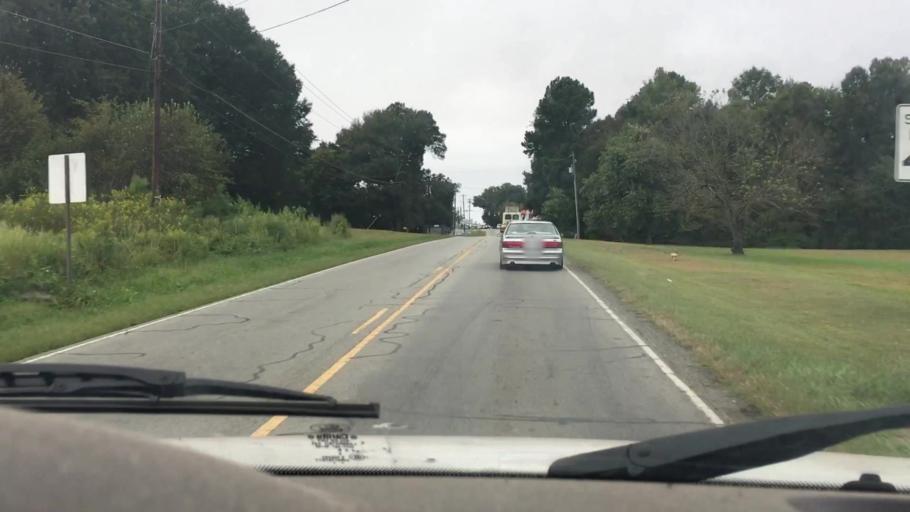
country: US
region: North Carolina
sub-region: Catawba County
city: Lake Norman of Catawba
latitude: 35.5904
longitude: -80.9742
